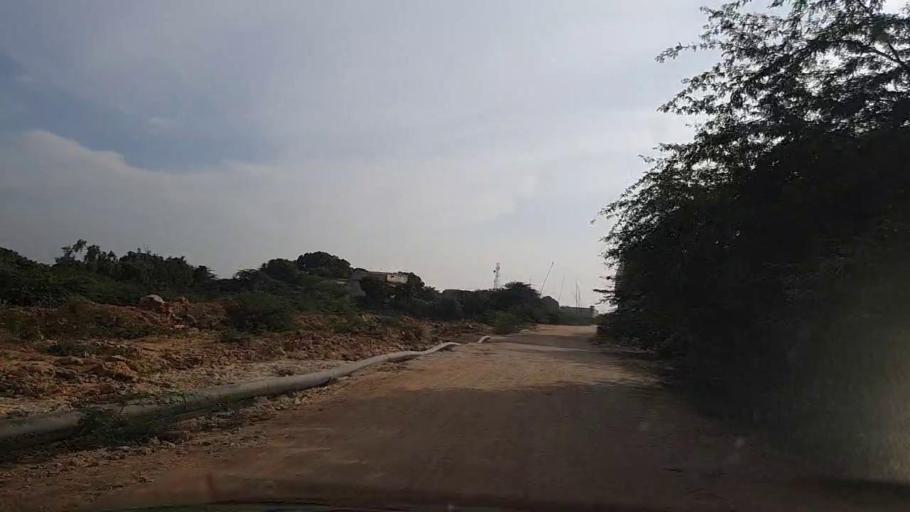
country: PK
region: Sindh
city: Gharo
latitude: 24.7912
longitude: 67.5312
